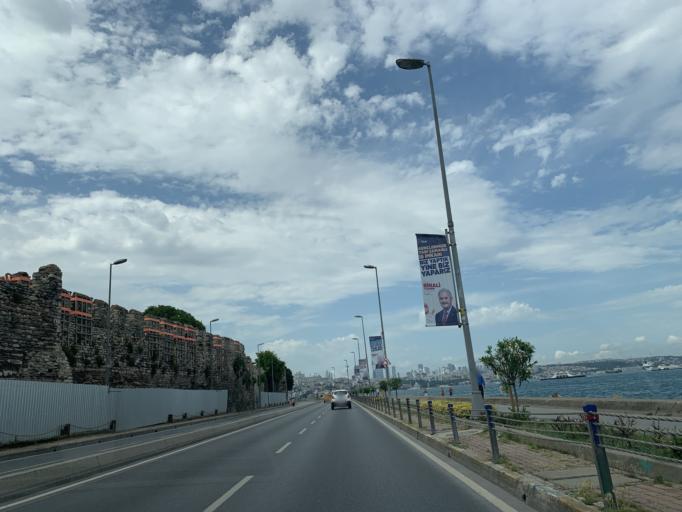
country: TR
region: Istanbul
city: Eminoenue
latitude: 41.0112
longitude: 28.9877
